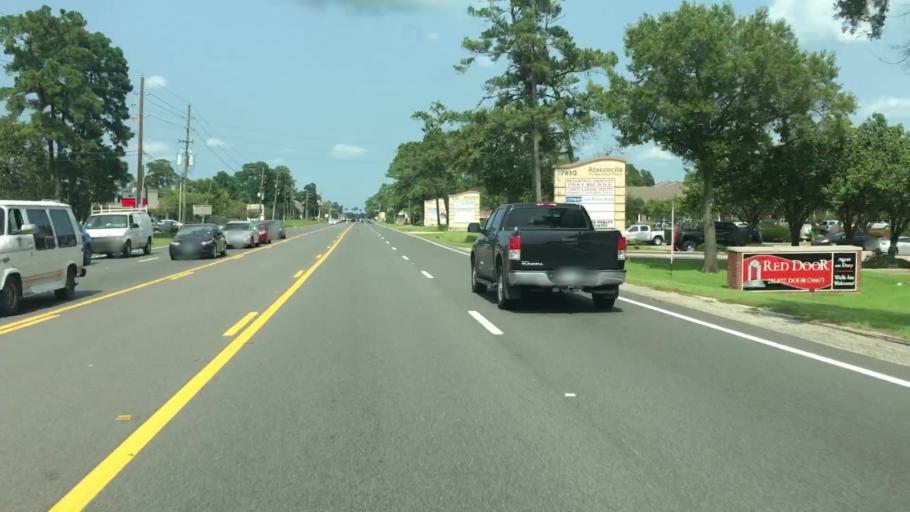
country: US
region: Texas
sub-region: Harris County
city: Atascocita
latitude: 30.0006
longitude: -95.1577
